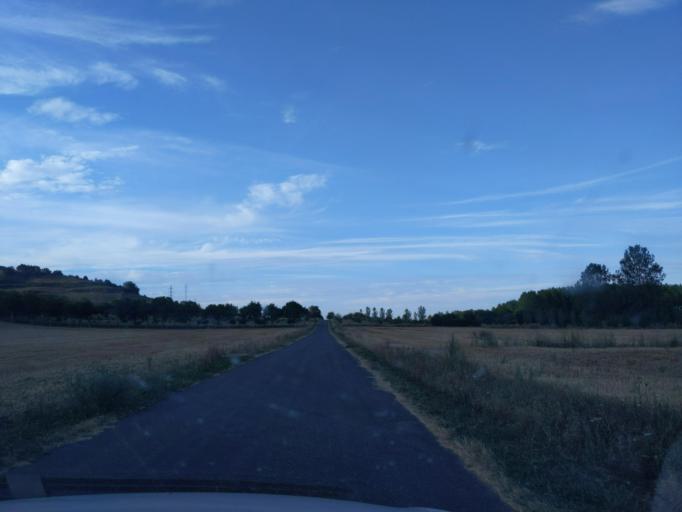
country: ES
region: La Rioja
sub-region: Provincia de La Rioja
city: Santurdejo
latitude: 42.3778
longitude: -2.9853
